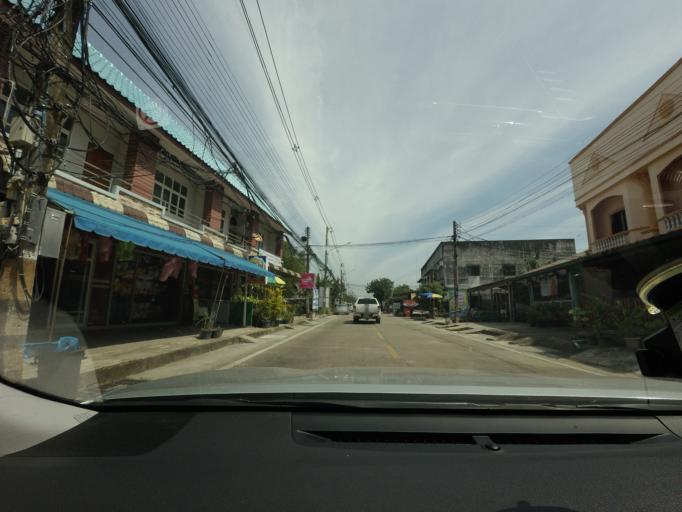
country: TH
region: Narathiwat
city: Narathiwat
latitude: 6.4239
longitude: 101.8152
